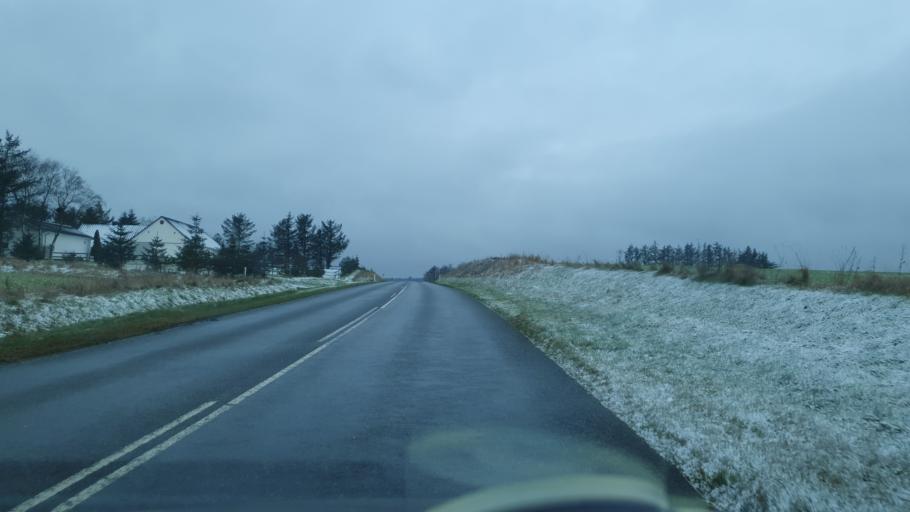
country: DK
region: North Denmark
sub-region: Jammerbugt Kommune
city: Brovst
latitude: 57.1260
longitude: 9.4841
